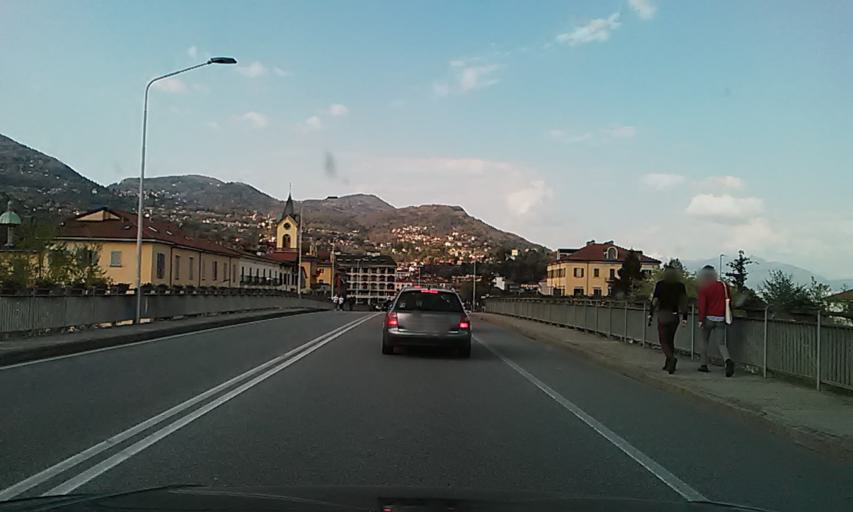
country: IT
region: Piedmont
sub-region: Provincia Verbano-Cusio-Ossola
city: Pallanza-Intra-Suna
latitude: 45.9322
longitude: 8.5709
